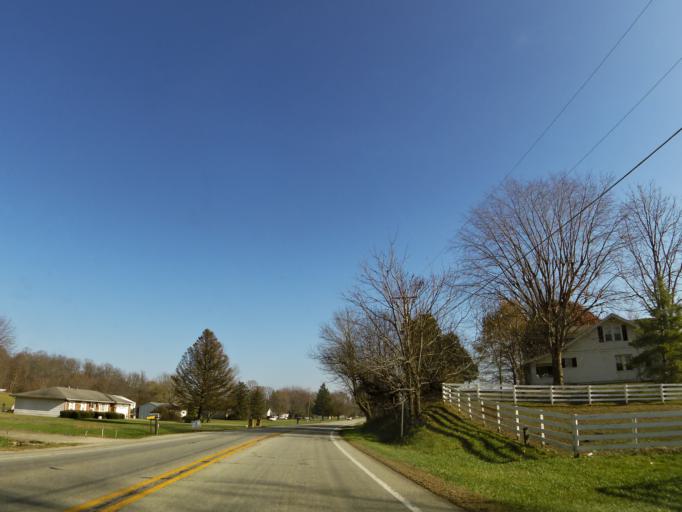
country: US
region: Indiana
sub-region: Fayette County
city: Connersville
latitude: 39.6335
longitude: -85.2116
